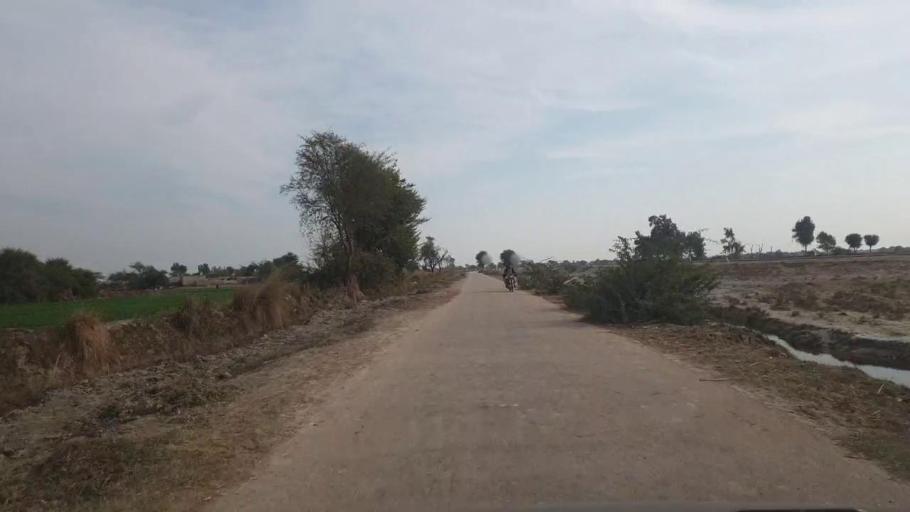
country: PK
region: Sindh
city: Nawabshah
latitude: 26.0889
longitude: 68.4853
